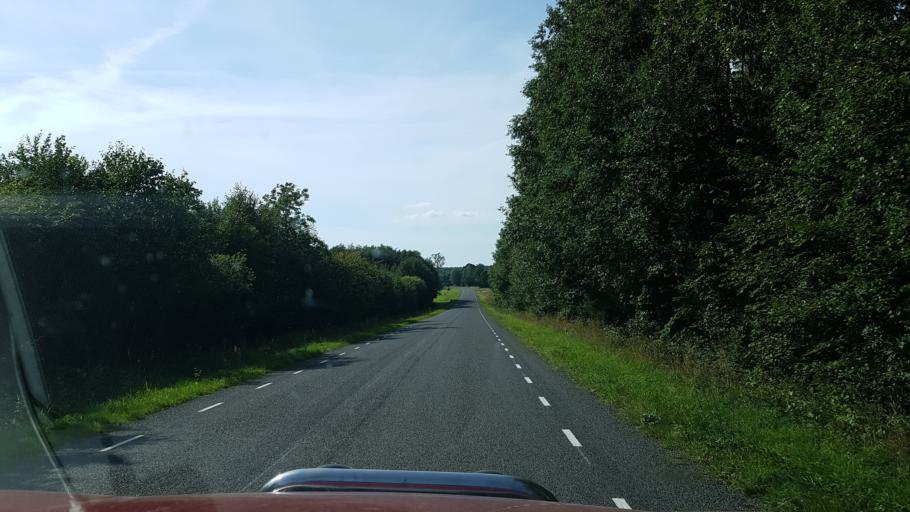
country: EE
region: Viljandimaa
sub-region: Abja vald
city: Abja-Paluoja
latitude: 58.3380
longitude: 25.2497
